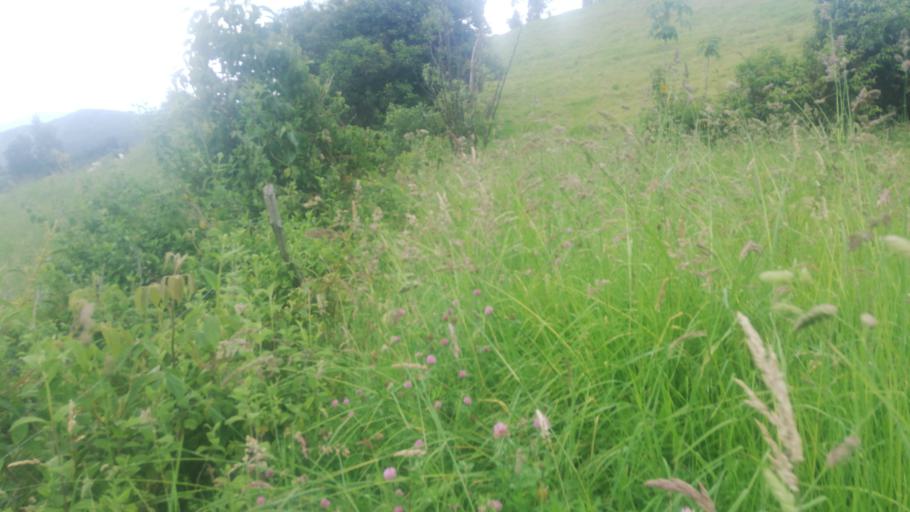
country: CO
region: Boyaca
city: Socha Viejo
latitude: 6.0733
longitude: -72.7299
